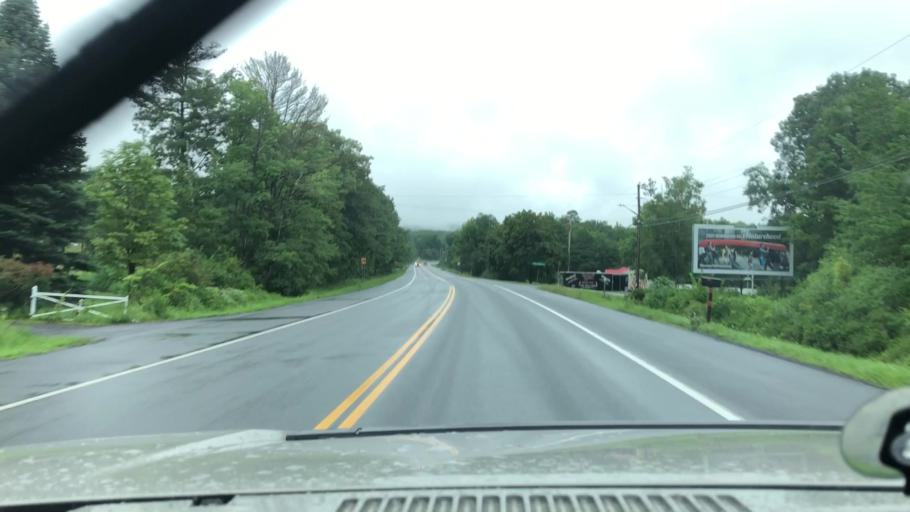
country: US
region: New York
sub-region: Greene County
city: Cairo
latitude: 42.3199
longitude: -74.0821
